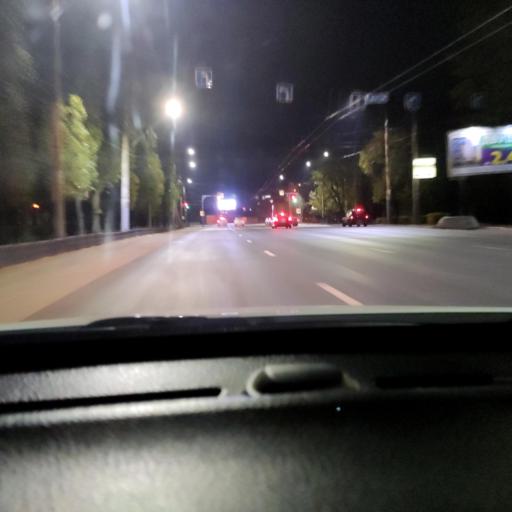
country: RU
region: Voronezj
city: Voronezh
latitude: 51.6320
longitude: 39.2297
